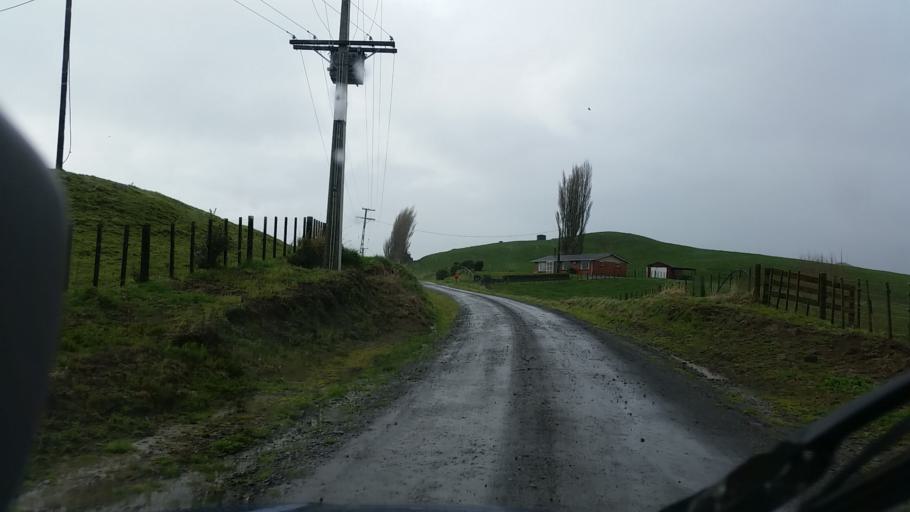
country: NZ
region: Taranaki
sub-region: South Taranaki District
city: Eltham
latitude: -39.3510
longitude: 174.4356
